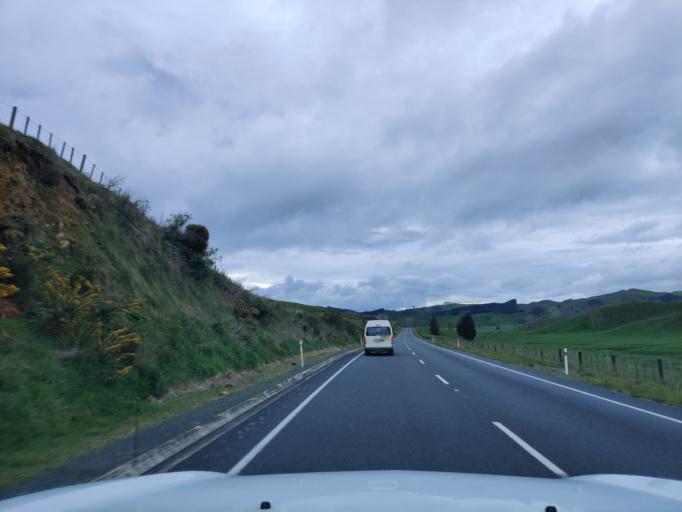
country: NZ
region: Waikato
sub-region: Otorohanga District
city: Otorohanga
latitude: -38.4644
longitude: 175.1681
